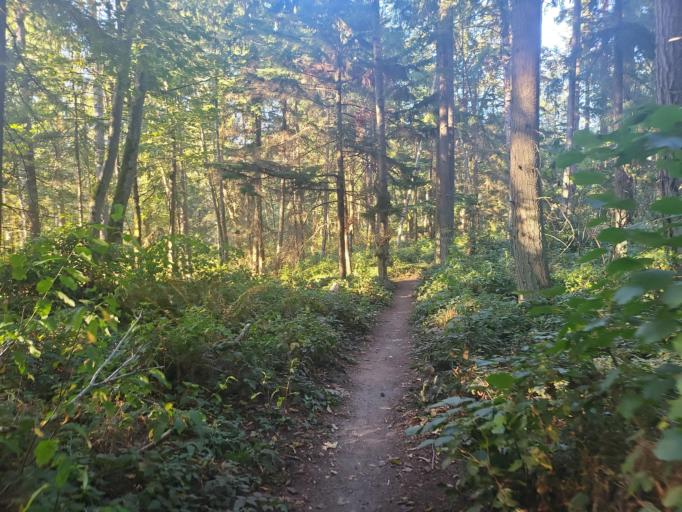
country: US
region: Washington
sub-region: Pierce County
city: Tacoma
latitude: 47.3138
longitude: -122.4086
